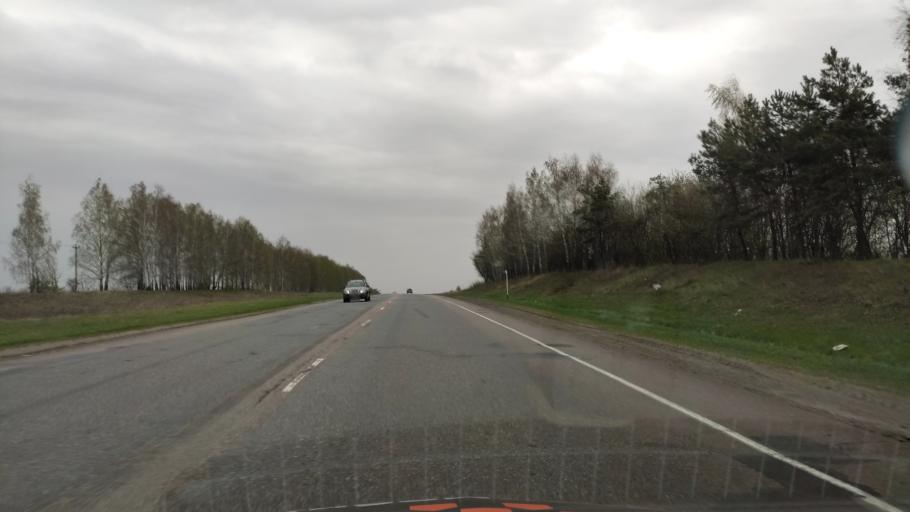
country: RU
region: Kursk
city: Gorshechnoye
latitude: 51.4510
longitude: 37.9160
